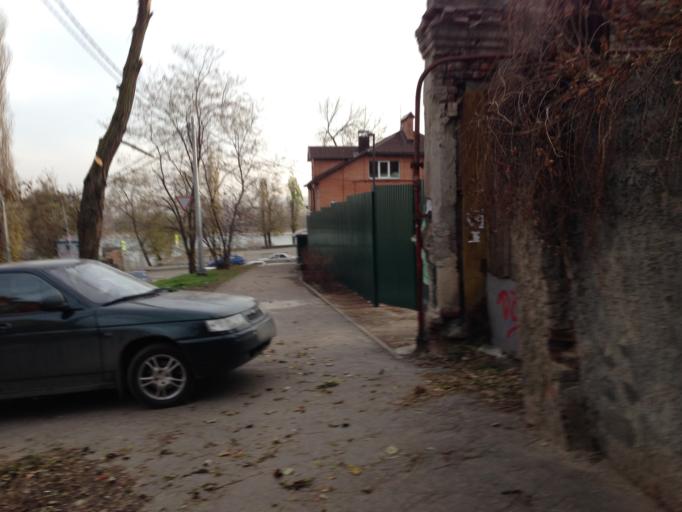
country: RU
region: Rostov
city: Rostov-na-Donu
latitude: 47.2192
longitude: 39.7258
